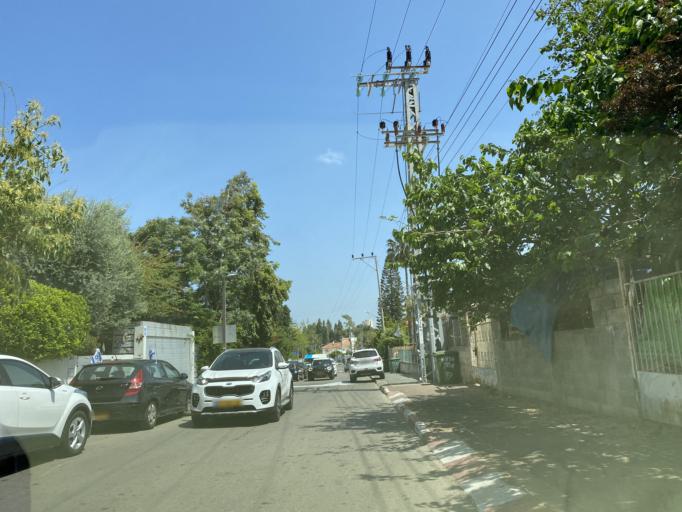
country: IL
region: Tel Aviv
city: Ramat HaSharon
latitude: 32.1537
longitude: 34.8363
